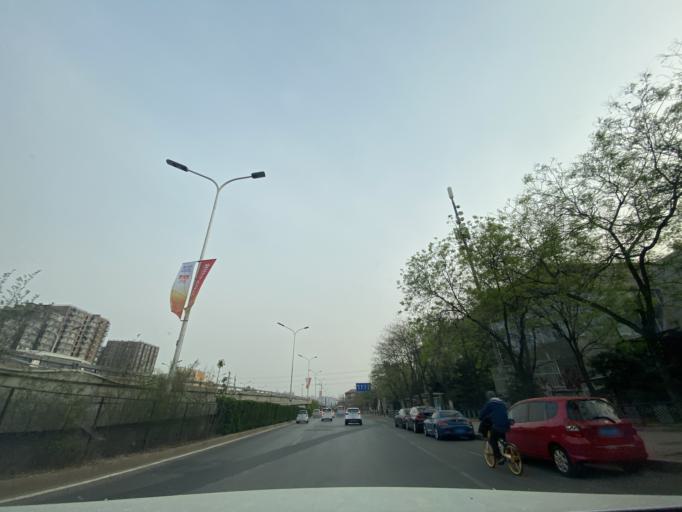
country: CN
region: Beijing
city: Sijiqing
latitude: 39.9289
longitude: 116.2688
